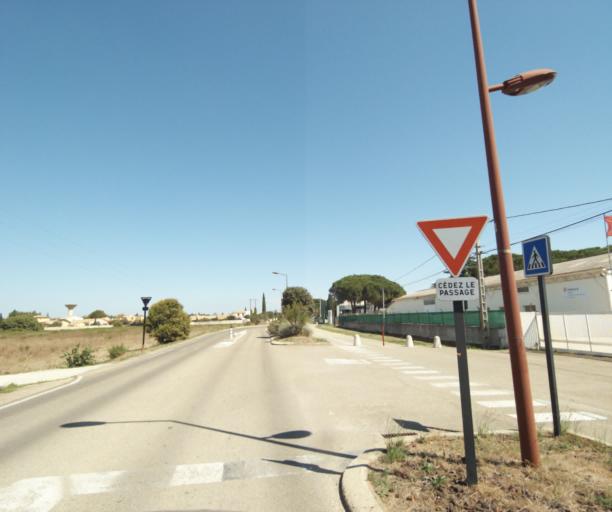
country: FR
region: Languedoc-Roussillon
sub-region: Departement du Gard
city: Rodilhan
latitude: 43.8227
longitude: 4.4304
